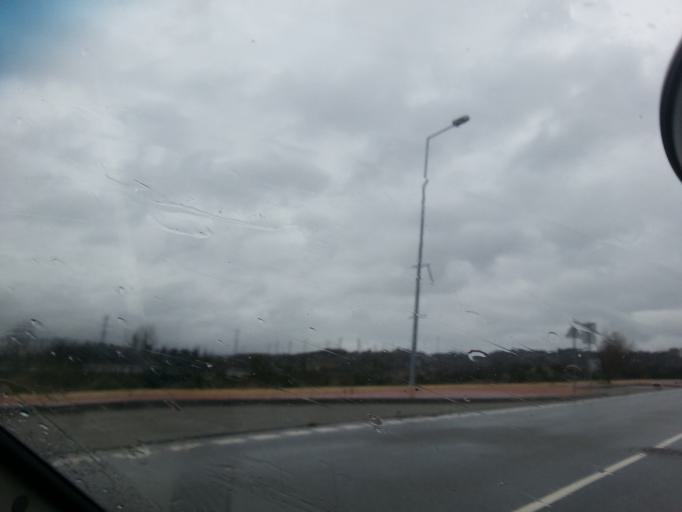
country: PT
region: Guarda
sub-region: Celorico da Beira
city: Celorico da Beira
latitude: 40.6270
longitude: -7.4201
